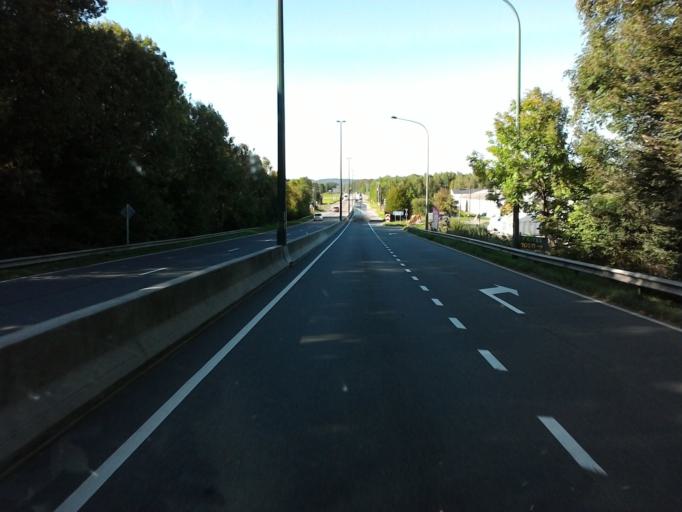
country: BE
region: Wallonia
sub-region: Province du Luxembourg
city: Attert
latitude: 49.7215
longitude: 5.7991
